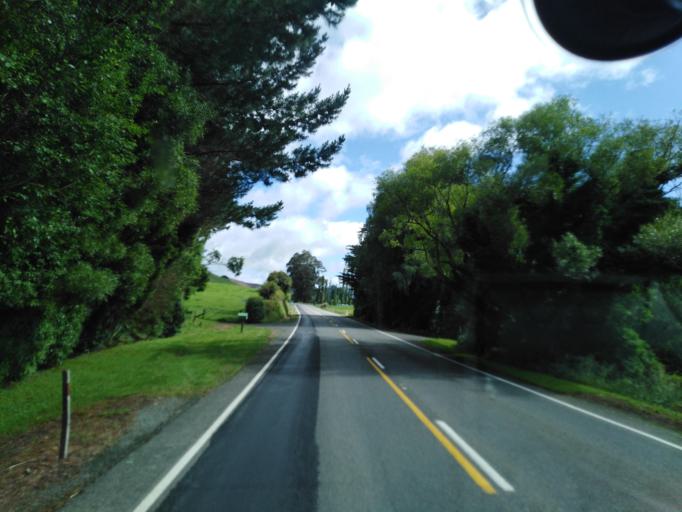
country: NZ
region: Nelson
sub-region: Nelson City
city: Nelson
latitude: -41.2798
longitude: 173.5736
